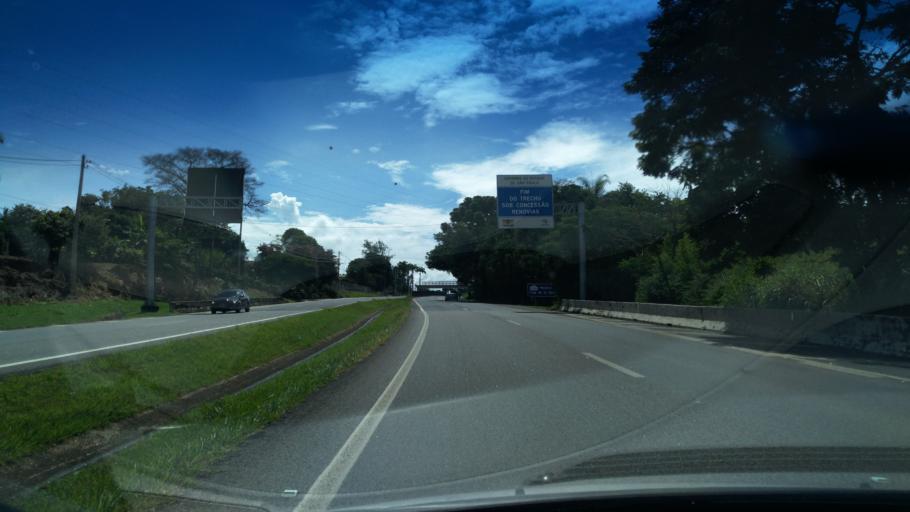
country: BR
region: Sao Paulo
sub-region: Santo Antonio Do Jardim
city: Espirito Santo do Pinhal
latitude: -22.1892
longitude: -46.7671
